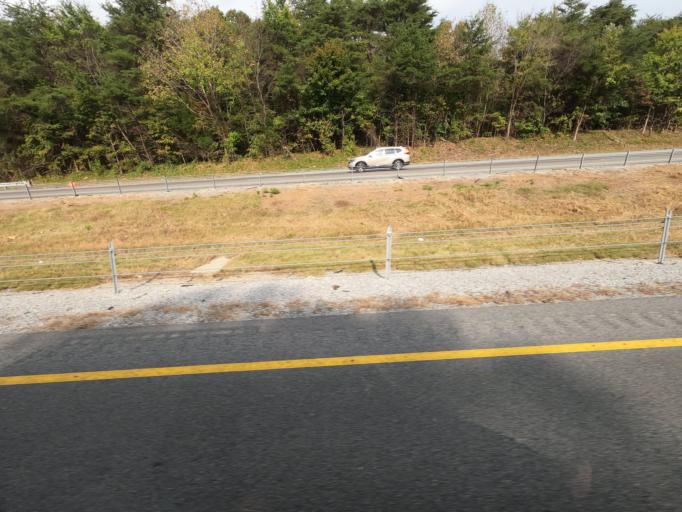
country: US
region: Tennessee
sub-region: Williamson County
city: Fairview
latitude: 36.0241
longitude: -87.1840
